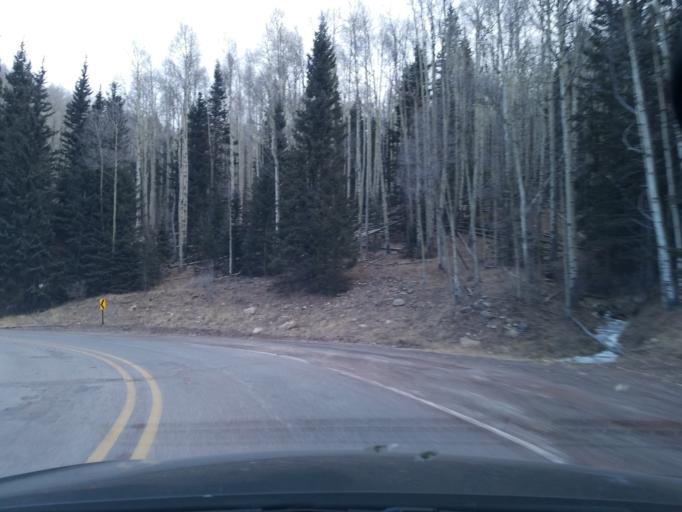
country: US
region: New Mexico
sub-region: Santa Fe County
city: Santa Fe
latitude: 35.7851
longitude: -105.8051
